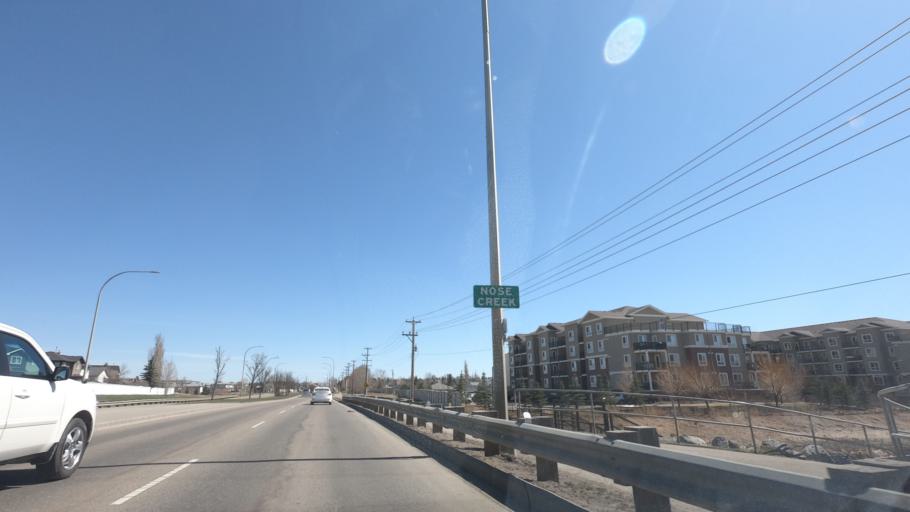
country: CA
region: Alberta
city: Airdrie
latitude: 51.2999
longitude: -114.0227
